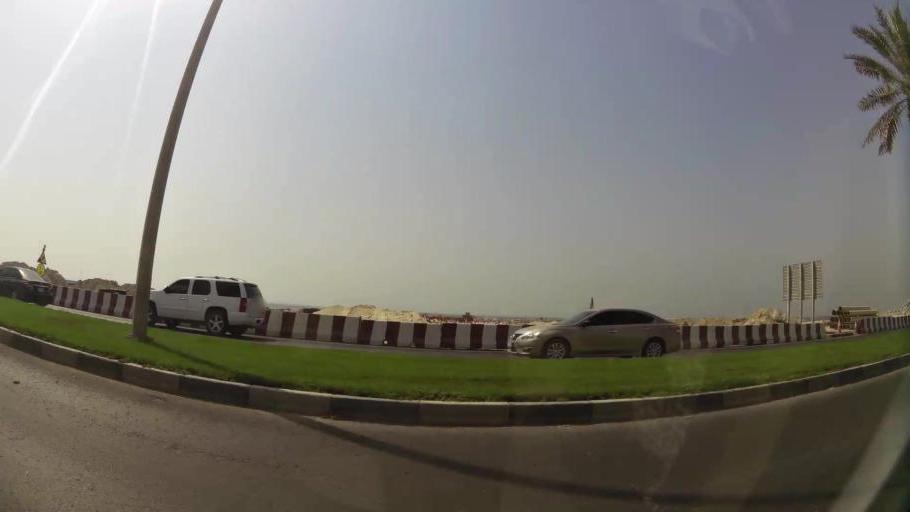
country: AE
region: Ajman
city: Ajman
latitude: 25.3895
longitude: 55.4149
